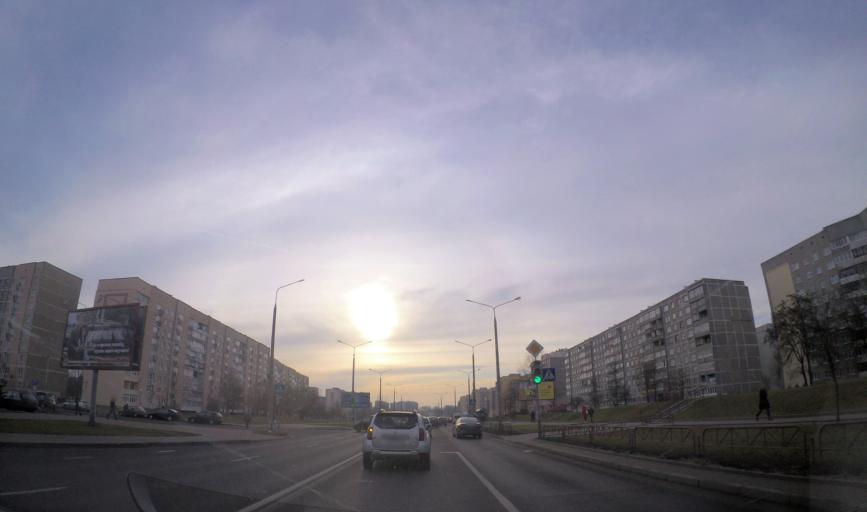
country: BY
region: Grodnenskaya
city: Hrodna
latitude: 53.6635
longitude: 23.7838
